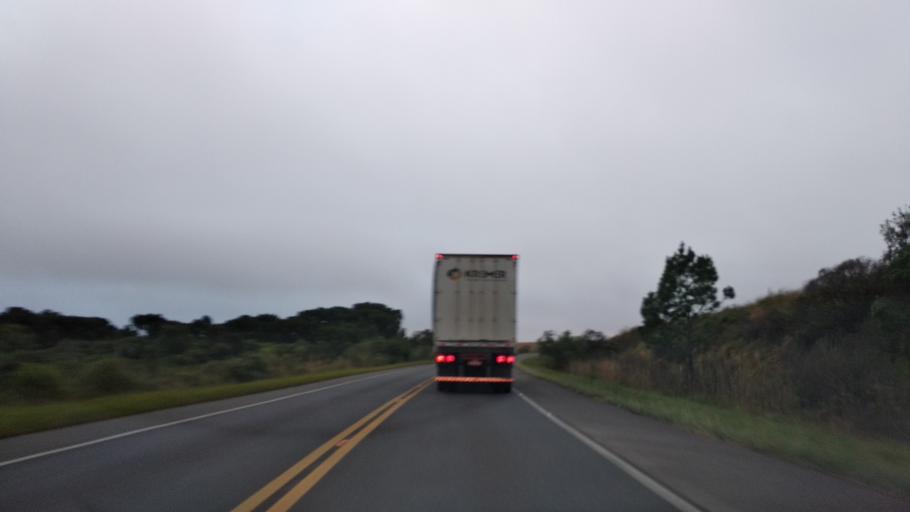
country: BR
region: Santa Catarina
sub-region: Campos Novos
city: Campos Novos
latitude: -27.3759
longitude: -51.0897
